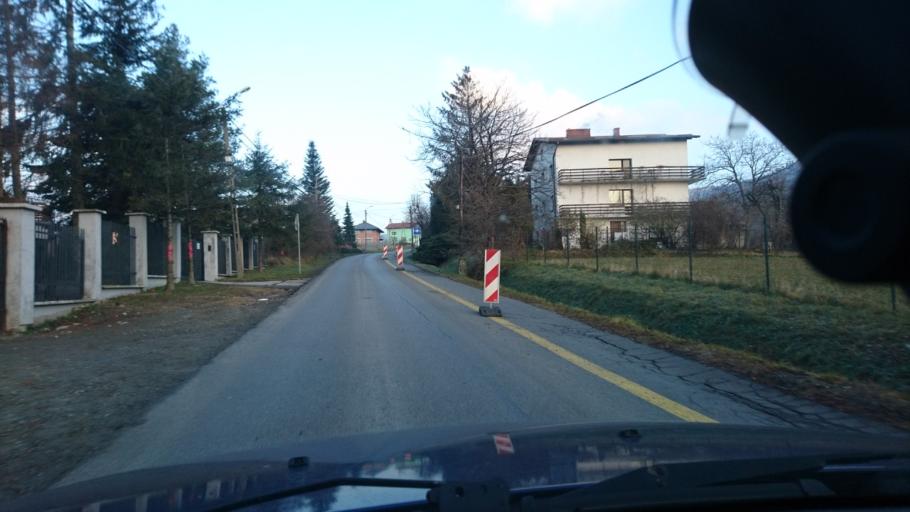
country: PL
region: Silesian Voivodeship
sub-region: Powiat bielski
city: Kozy
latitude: 49.8209
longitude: 19.1022
